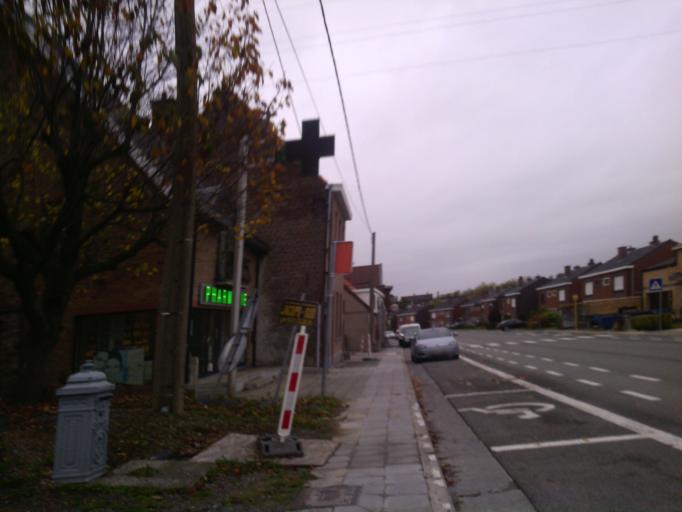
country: BE
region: Wallonia
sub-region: Province du Hainaut
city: Mouscron
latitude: 50.7620
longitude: 3.2194
